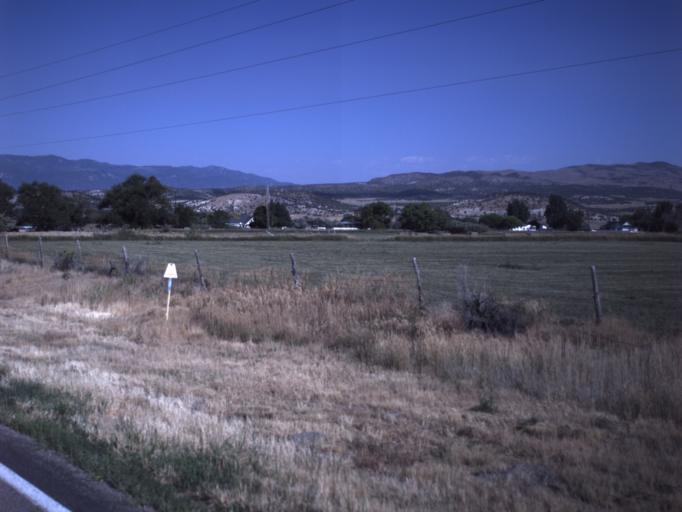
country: US
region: Utah
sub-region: Sanpete County
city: Mount Pleasant
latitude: 39.5468
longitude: -111.4715
